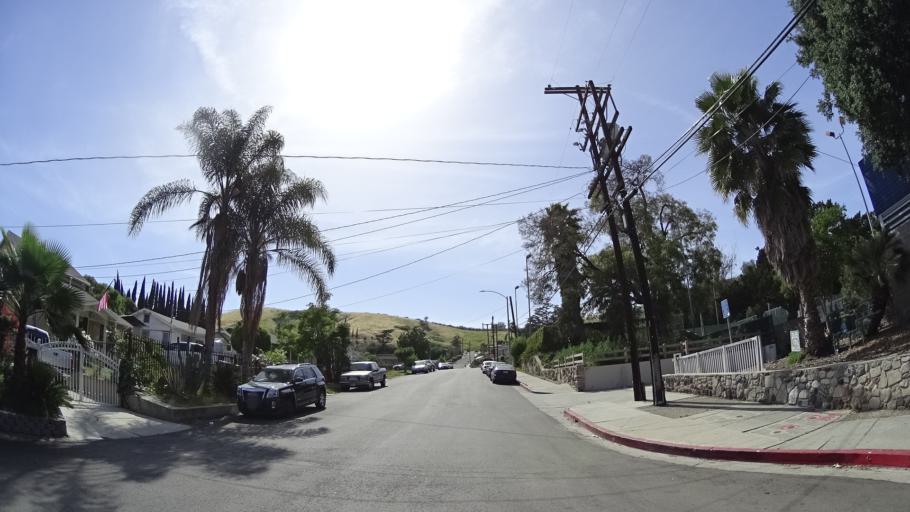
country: US
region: California
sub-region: Los Angeles County
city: Belvedere
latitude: 34.0757
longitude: -118.1815
